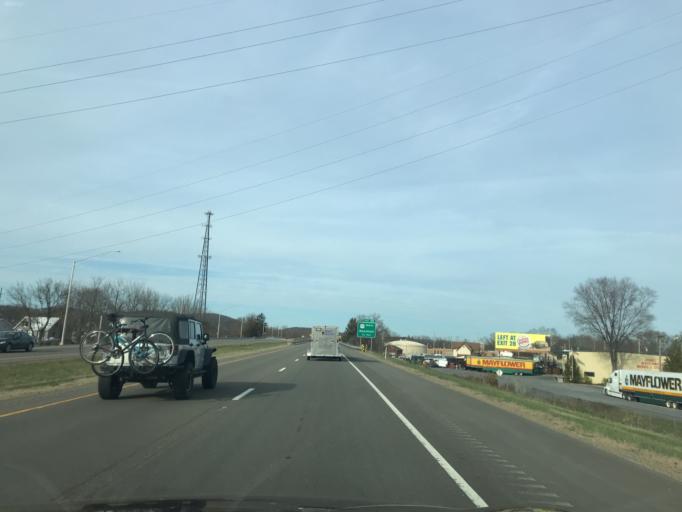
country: US
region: Pennsylvania
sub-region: Lycoming County
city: Duboistown
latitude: 41.2270
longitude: -77.0490
